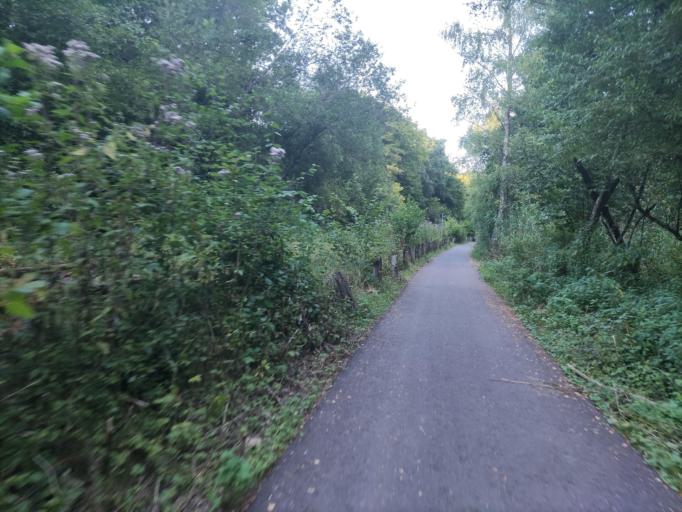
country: DE
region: Saarland
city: Wadgassen
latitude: 49.2552
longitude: 6.7954
